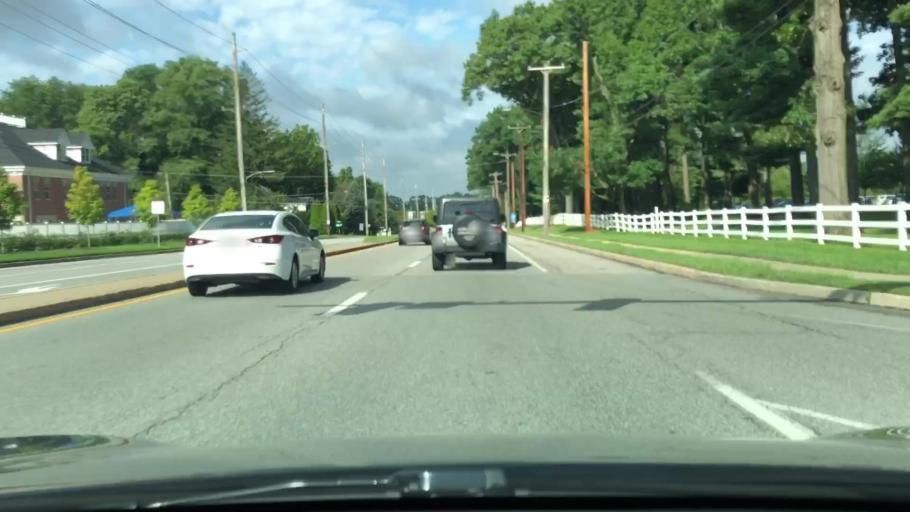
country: US
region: Pennsylvania
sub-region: Delaware County
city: Broomall
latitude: 39.9862
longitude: -75.4090
